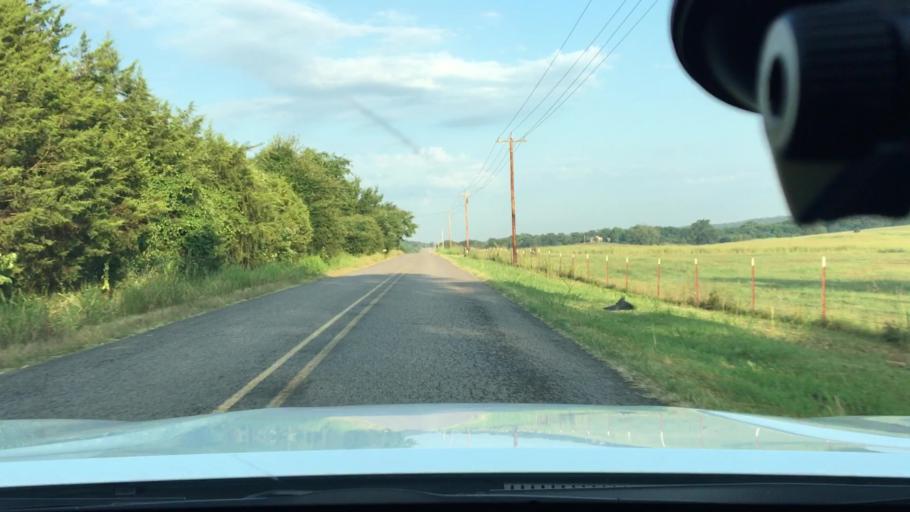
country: US
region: Arkansas
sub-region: Johnson County
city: Coal Hill
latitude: 35.3663
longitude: -93.5986
